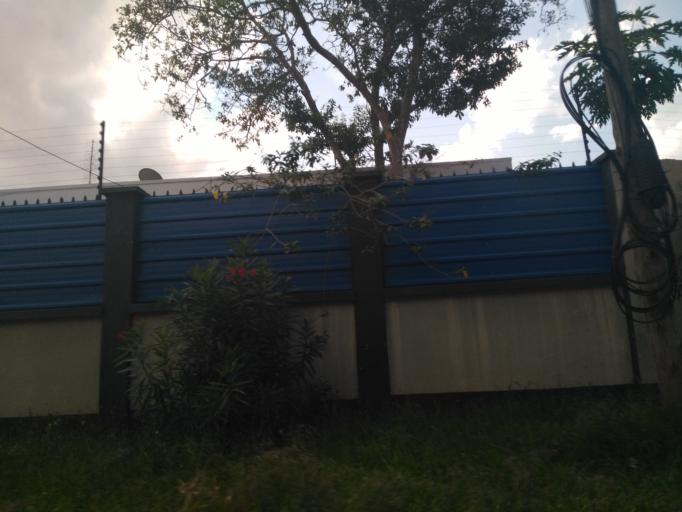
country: TZ
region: Dar es Salaam
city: Magomeni
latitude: -6.7754
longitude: 39.2568
